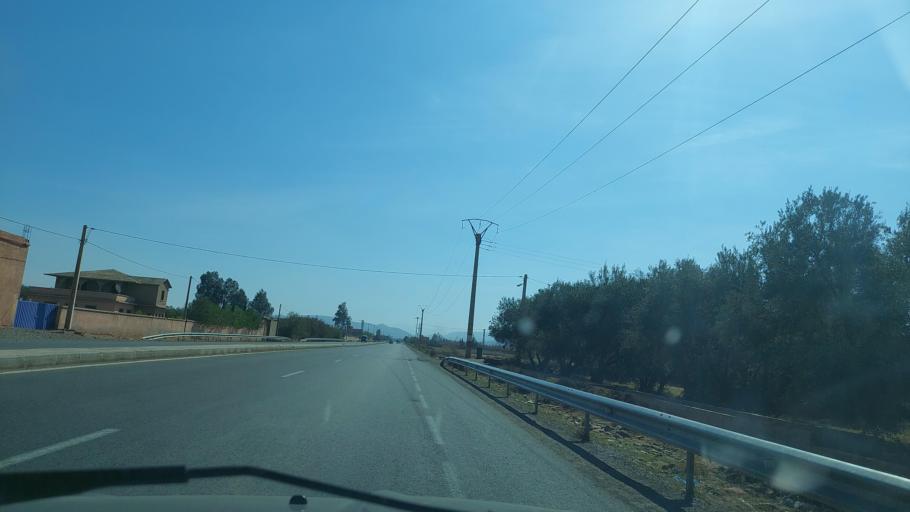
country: MA
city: Sidi Abdallah Ghiat
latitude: 31.5649
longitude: -7.7192
